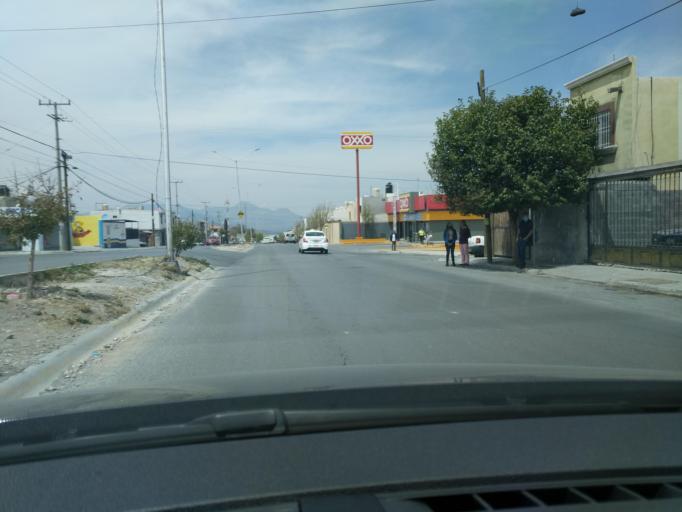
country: MX
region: Coahuila
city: Saltillo
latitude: 25.3556
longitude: -101.0172
